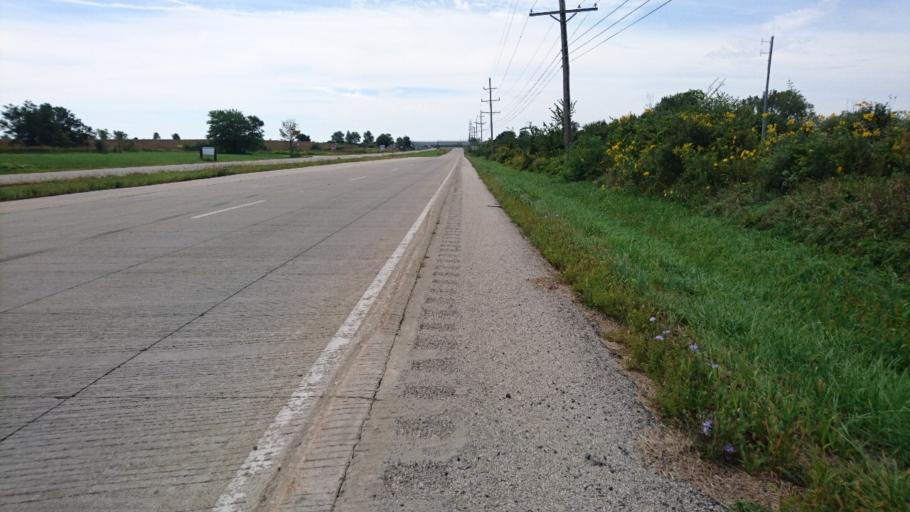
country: US
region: Illinois
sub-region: Will County
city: Elwood
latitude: 41.3798
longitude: -88.1267
